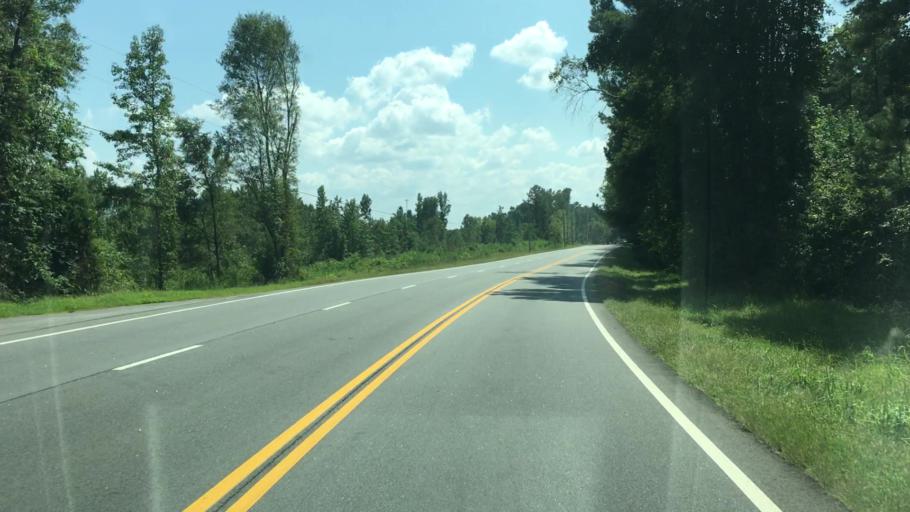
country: US
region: Georgia
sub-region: Oconee County
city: Watkinsville
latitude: 33.7376
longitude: -83.4289
